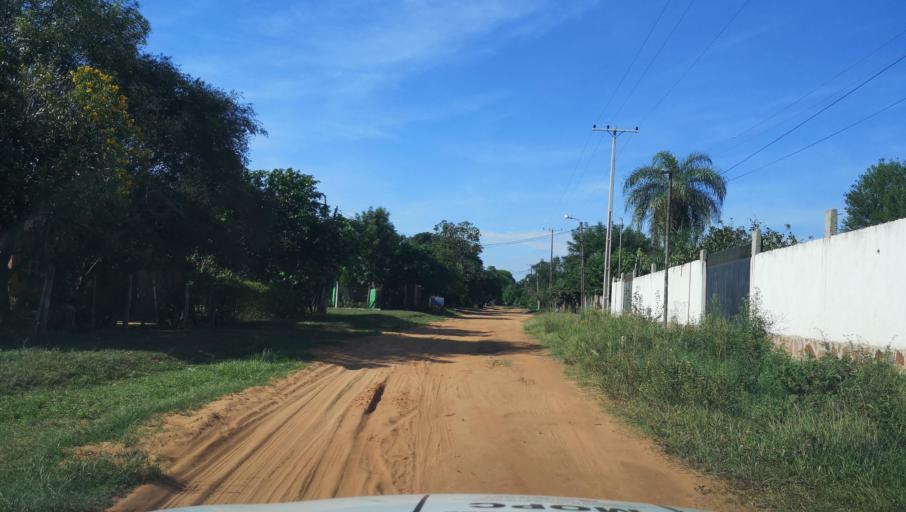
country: PY
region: Misiones
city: Santa Maria
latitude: -26.8745
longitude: -57.0086
